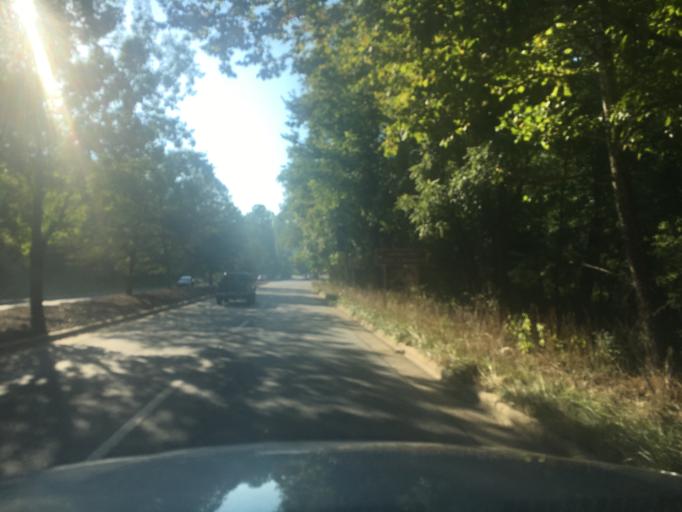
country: US
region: North Carolina
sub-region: Buncombe County
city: Asheville
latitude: 35.6129
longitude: -82.5688
